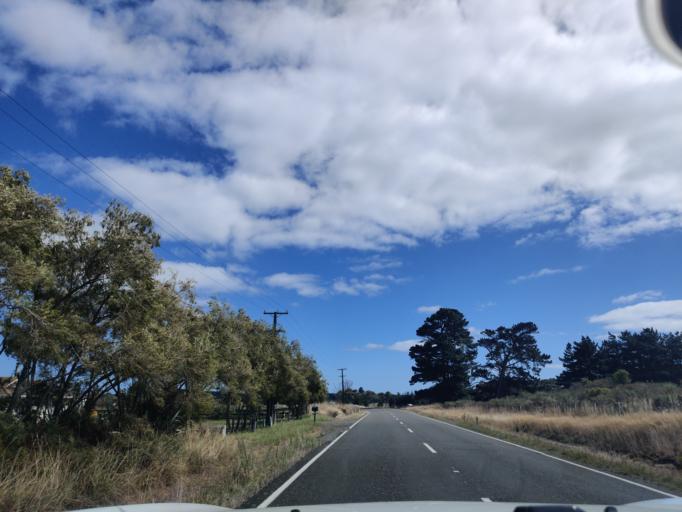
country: NZ
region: Manawatu-Wanganui
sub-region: Horowhenua District
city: Foxton
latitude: -40.3832
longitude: 175.2742
